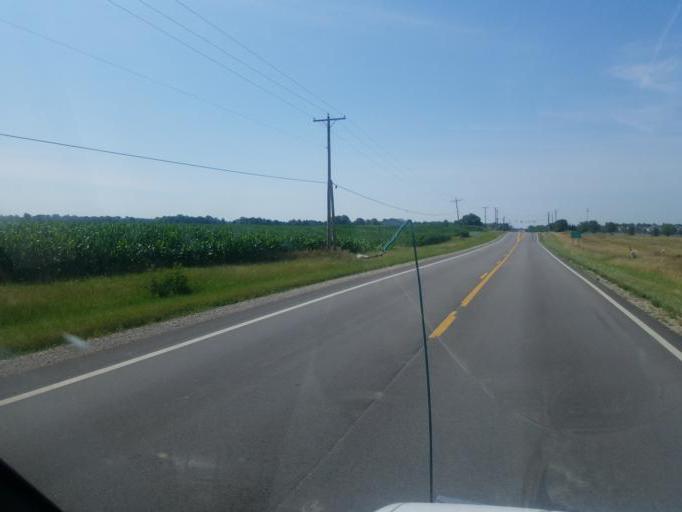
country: US
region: Ohio
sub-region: Union County
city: Marysville
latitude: 40.2720
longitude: -83.3754
